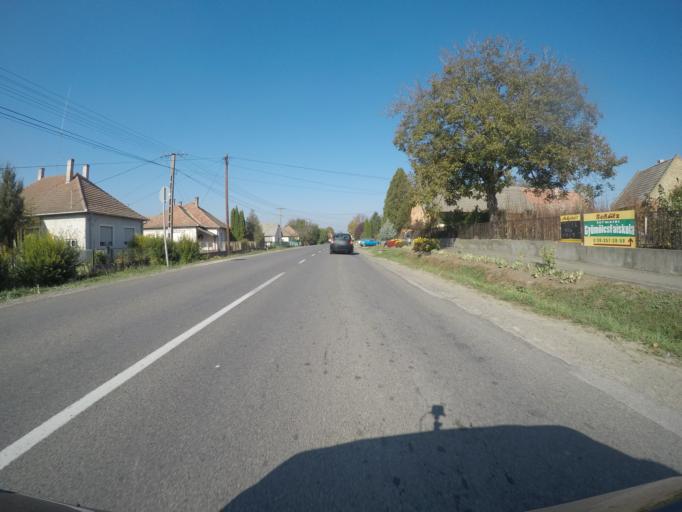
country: HU
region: Tolna
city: Szedres
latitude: 46.4708
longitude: 18.6856
